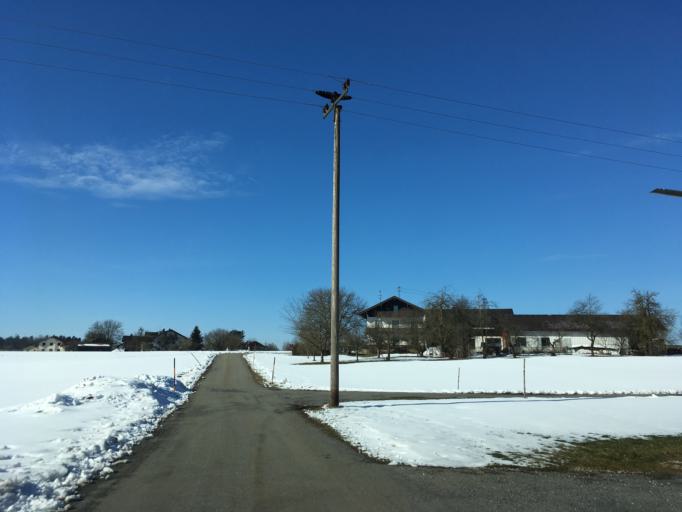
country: DE
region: Bavaria
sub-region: Upper Bavaria
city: Rechtmehring
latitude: 48.1105
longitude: 12.1546
